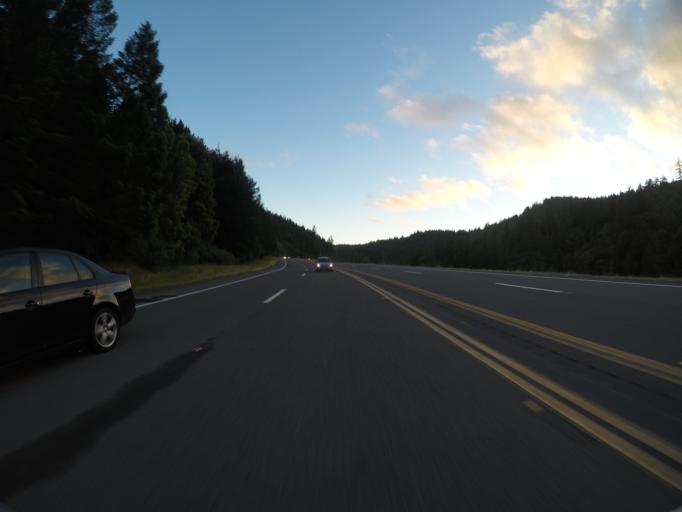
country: US
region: California
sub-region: Humboldt County
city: Redway
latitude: 39.9884
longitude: -123.7940
